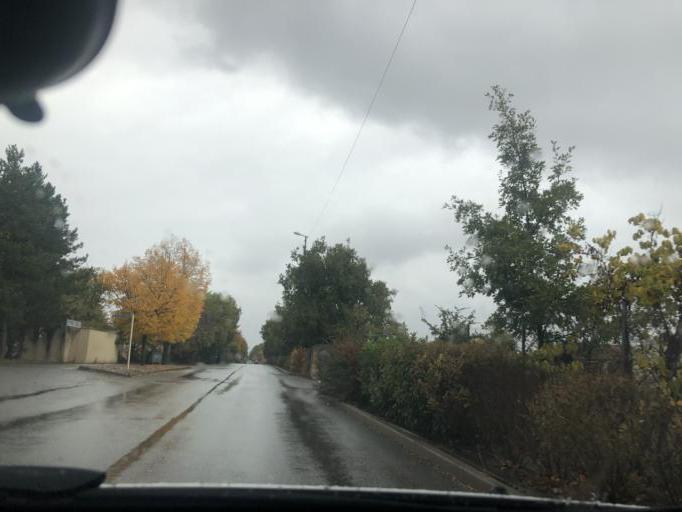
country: FR
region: Provence-Alpes-Cote d'Azur
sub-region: Departement des Alpes-de-Haute-Provence
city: Sisteron
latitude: 44.2265
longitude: 5.9136
